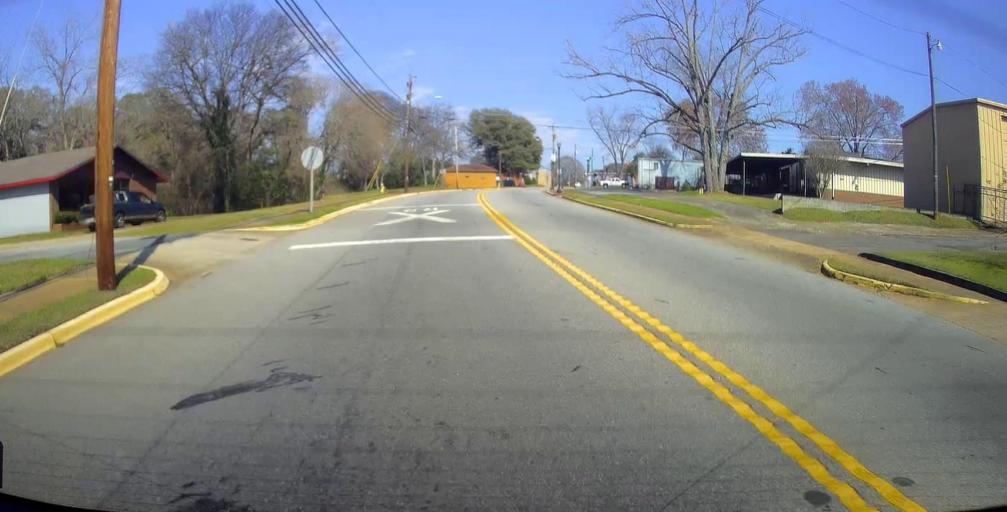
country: US
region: Georgia
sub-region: Houston County
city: Perry
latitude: 32.4579
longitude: -83.7367
